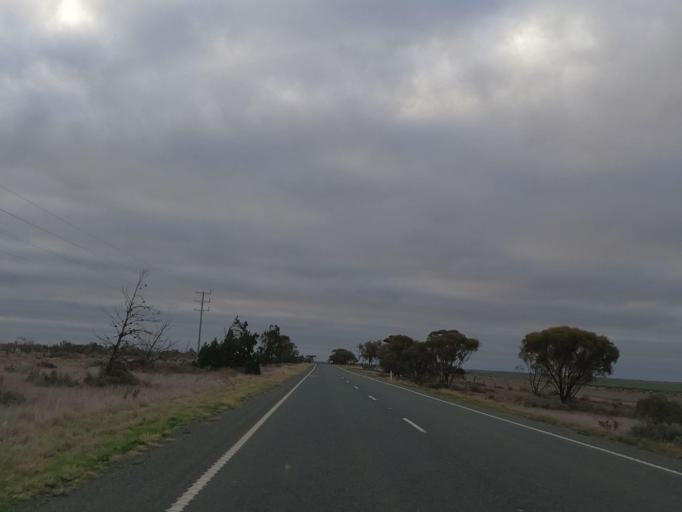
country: AU
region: Victoria
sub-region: Swan Hill
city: Swan Hill
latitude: -35.5723
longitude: 143.7865
